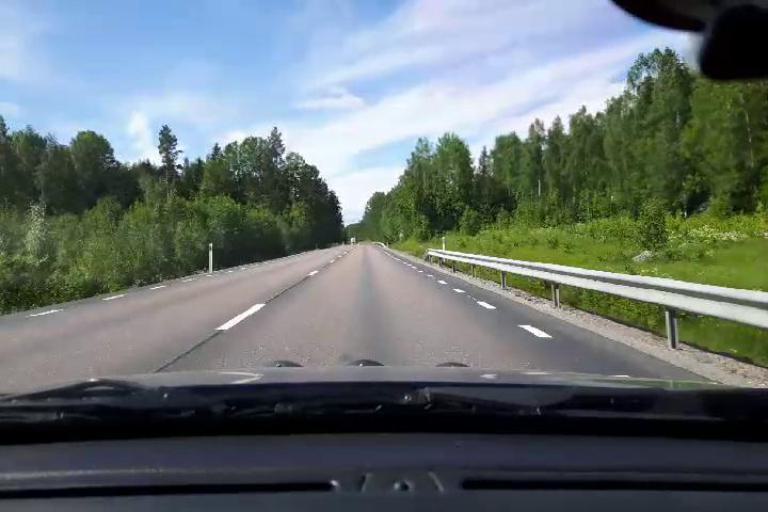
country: SE
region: Gaevleborg
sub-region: Bollnas Kommun
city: Kilafors
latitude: 61.1819
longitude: 16.7844
